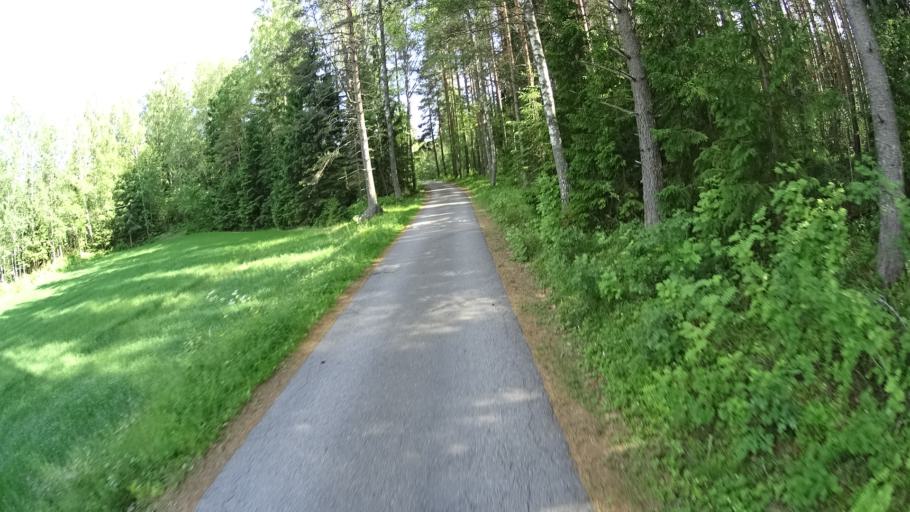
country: FI
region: Uusimaa
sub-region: Helsinki
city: Vantaa
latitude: 60.2357
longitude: 25.1827
